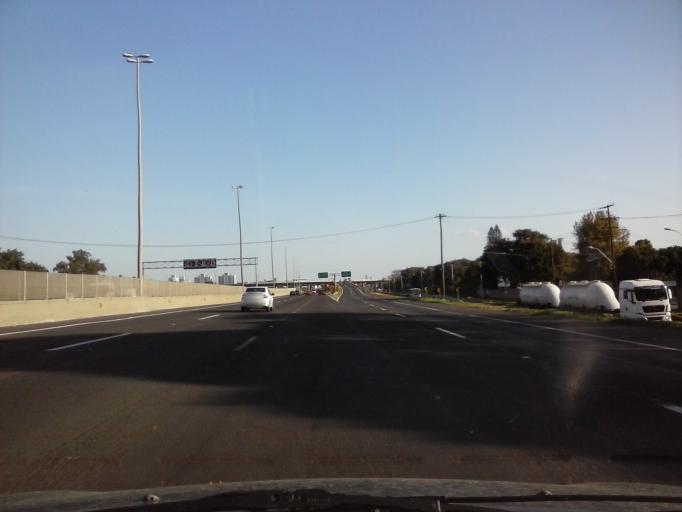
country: BR
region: Rio Grande do Sul
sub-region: Porto Alegre
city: Porto Alegre
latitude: -29.9926
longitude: -51.2050
